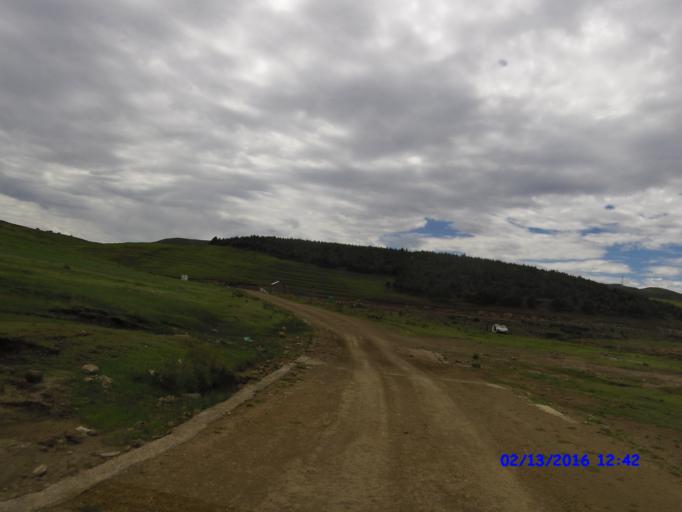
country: LS
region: Maseru
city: Nako
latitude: -29.8288
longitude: 28.0363
